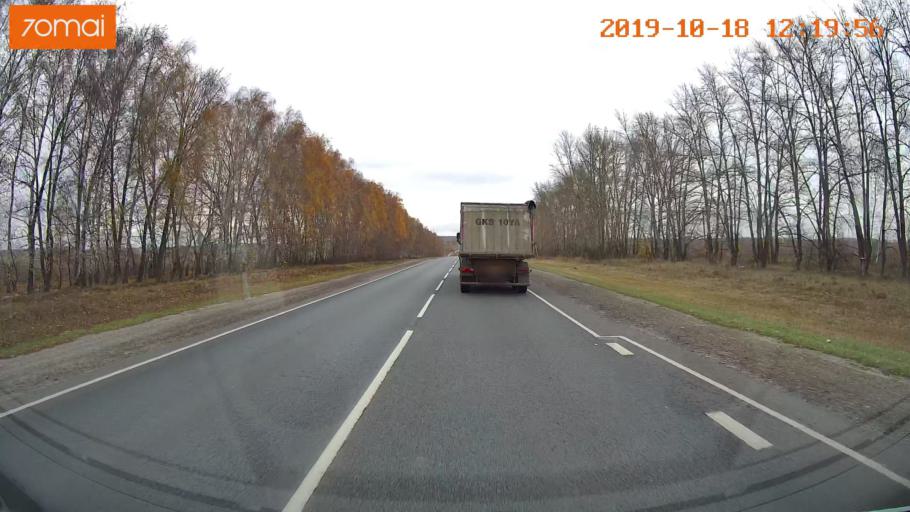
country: RU
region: Rjazan
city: Zakharovo
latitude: 54.4898
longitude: 39.4740
